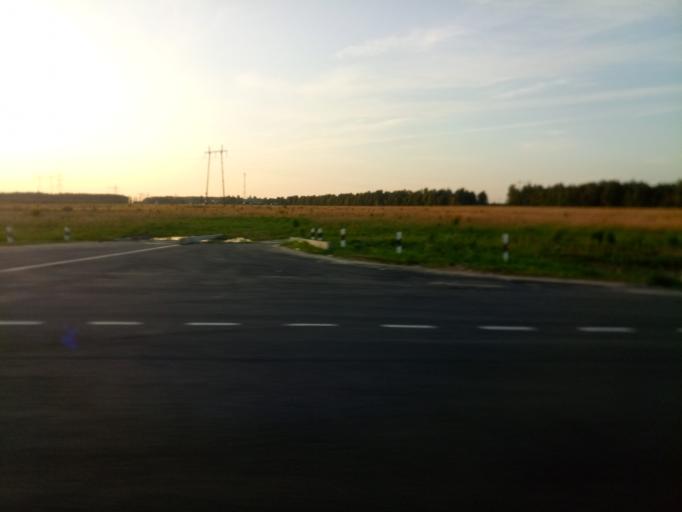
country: RU
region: Moskovskaya
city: Noginsk-9
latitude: 56.1116
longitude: 38.6105
